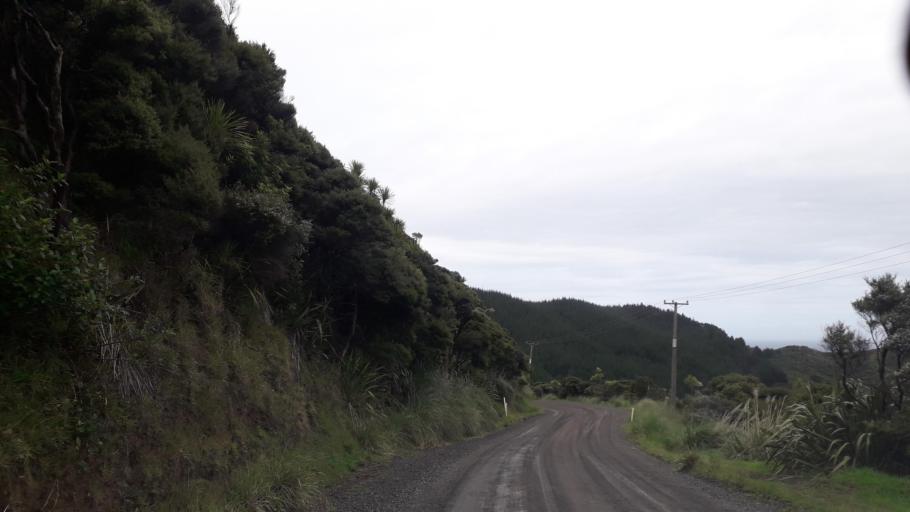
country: NZ
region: Northland
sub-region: Far North District
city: Ahipara
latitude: -35.4384
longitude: 173.3047
